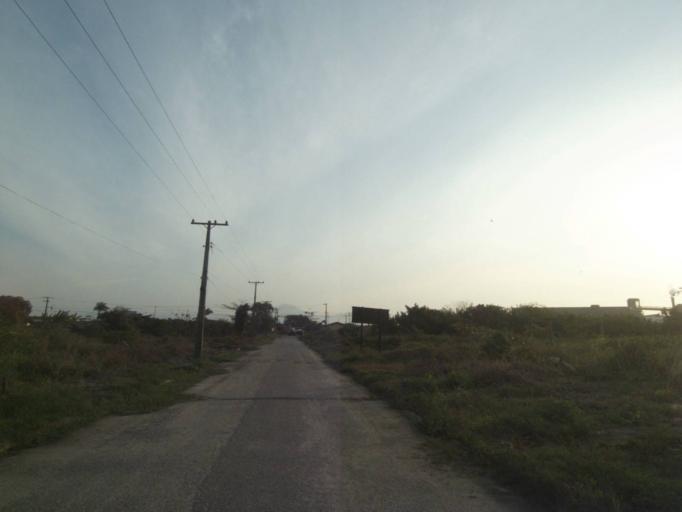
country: BR
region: Parana
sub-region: Paranagua
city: Paranagua
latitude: -25.5105
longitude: -48.5364
